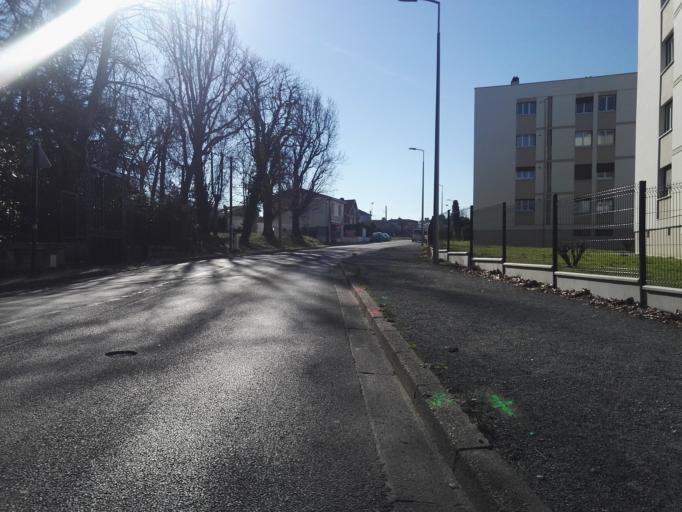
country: FR
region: Aquitaine
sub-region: Departement de la Gironde
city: Talence
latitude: 44.8013
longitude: -0.5851
